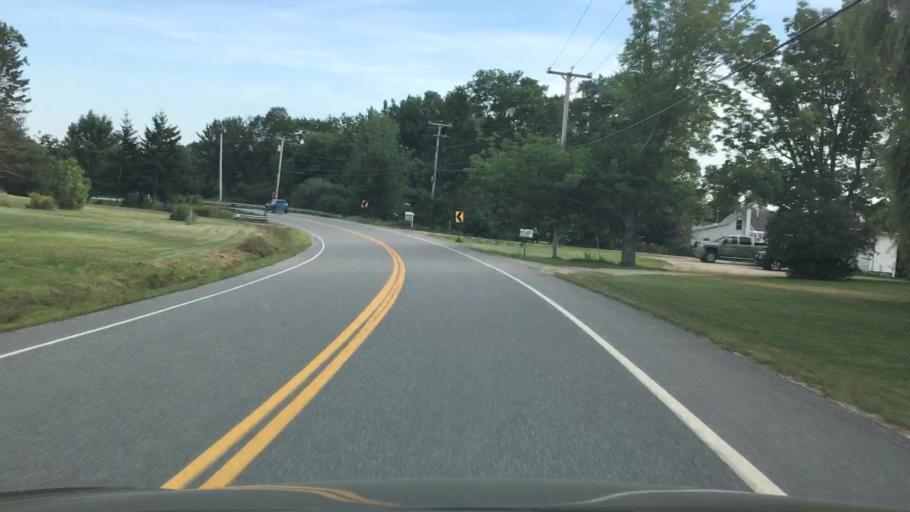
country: US
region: Maine
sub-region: Hancock County
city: Penobscot
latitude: 44.4628
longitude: -68.7827
